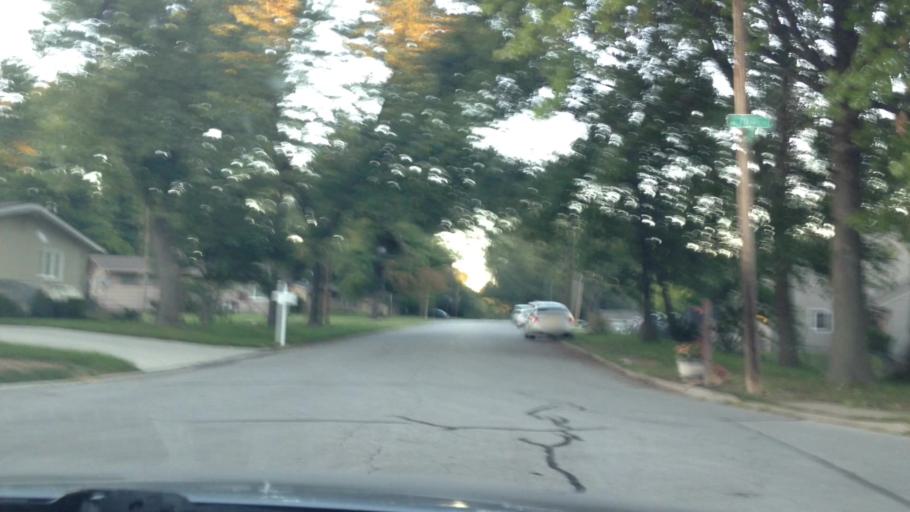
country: US
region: Missouri
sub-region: Platte County
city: Parkville
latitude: 39.2209
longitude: -94.6578
